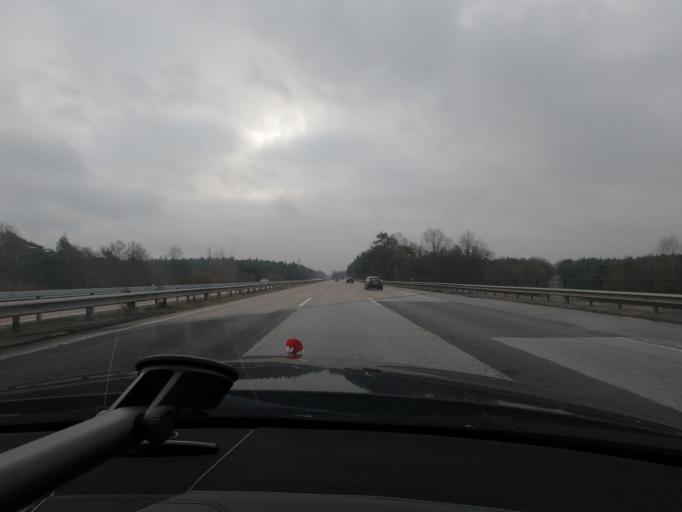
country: DE
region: Lower Saxony
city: Bispingen
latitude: 53.0587
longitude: 9.9540
